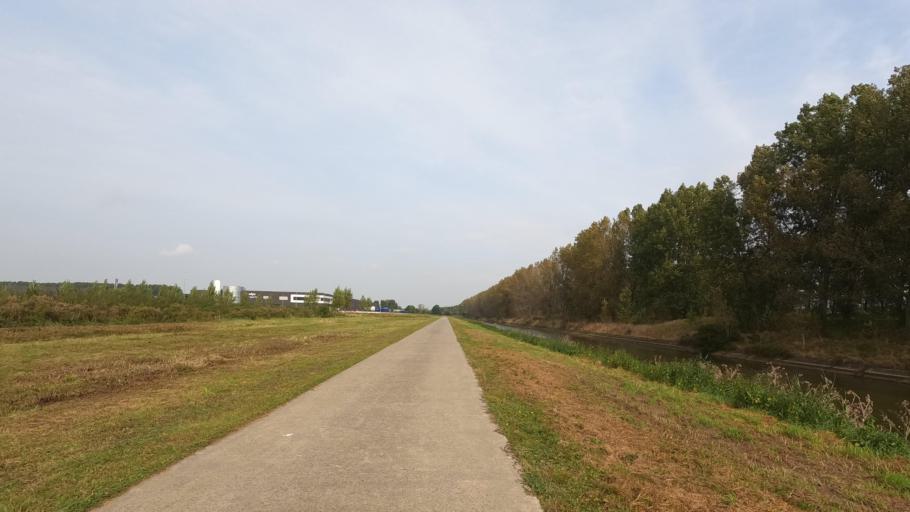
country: BE
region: Flanders
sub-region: Provincie Oost-Vlaanderen
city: Beveren
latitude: 51.2439
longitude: 4.2019
